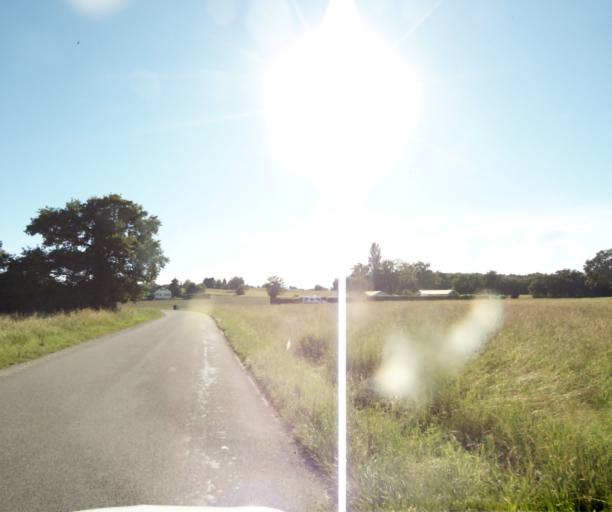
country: FR
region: Rhone-Alpes
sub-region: Departement de la Haute-Savoie
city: Massongy
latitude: 46.3523
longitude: 6.3355
